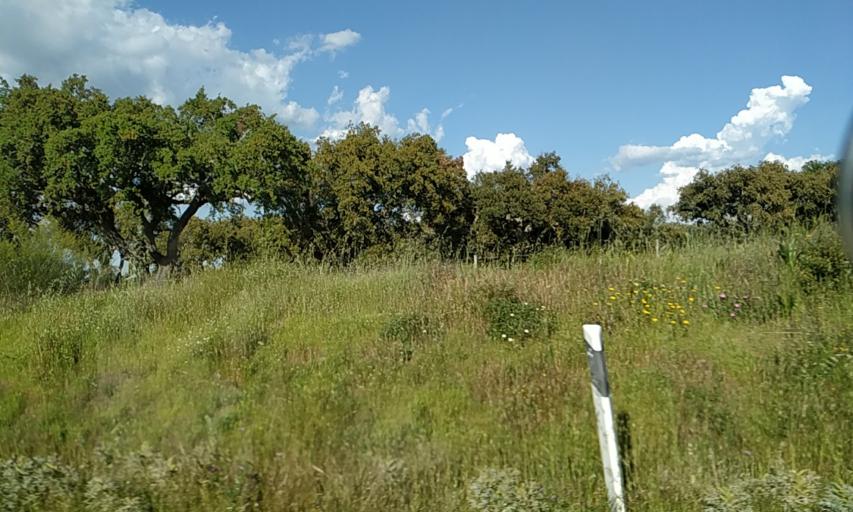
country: PT
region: Portalegre
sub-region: Portalegre
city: Urra
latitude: 39.1530
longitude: -7.4543
